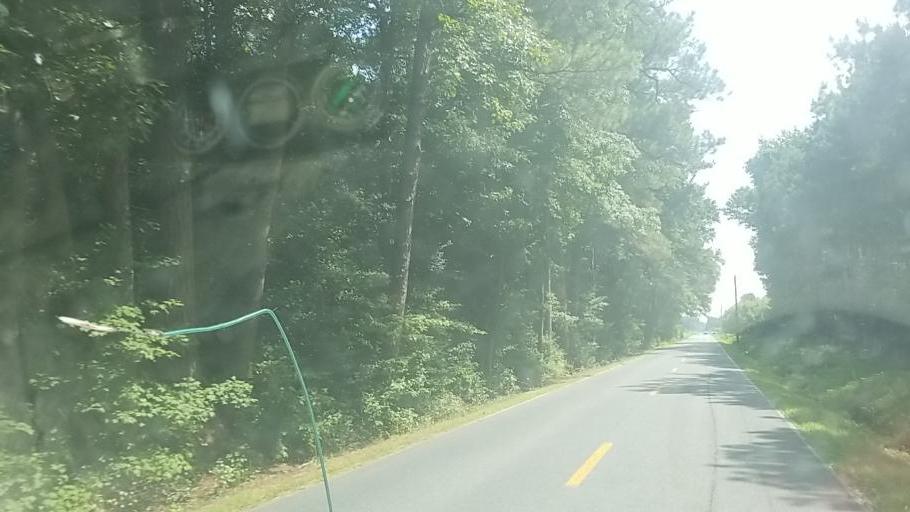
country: US
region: Maryland
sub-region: Wicomico County
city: Hebron
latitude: 38.4350
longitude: -75.6980
